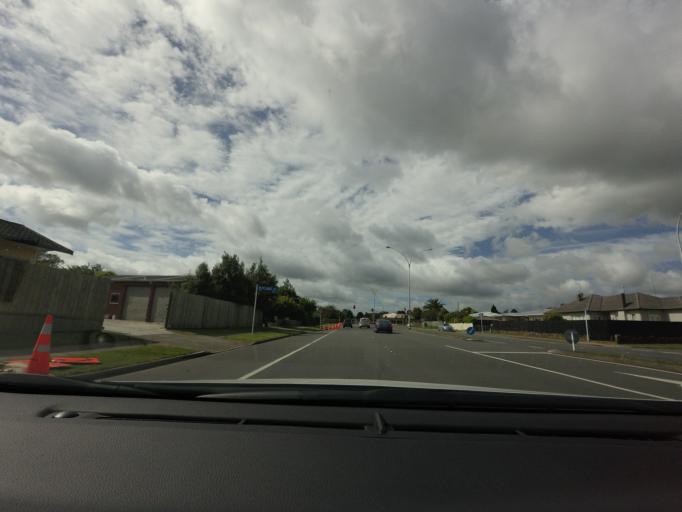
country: NZ
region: Bay of Plenty
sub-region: Rotorua District
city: Rotorua
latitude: -38.1436
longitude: 176.2375
